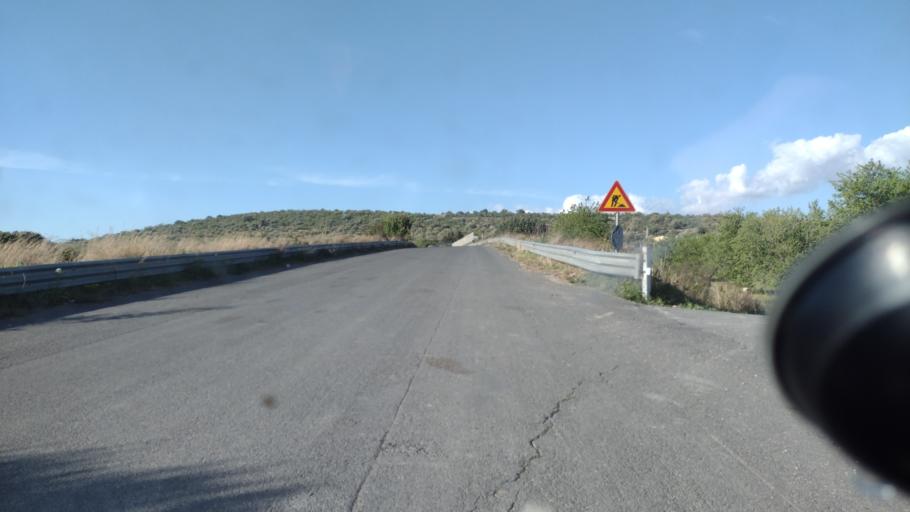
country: IT
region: Sicily
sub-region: Provincia di Siracusa
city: Noto
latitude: 36.8454
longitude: 15.0243
